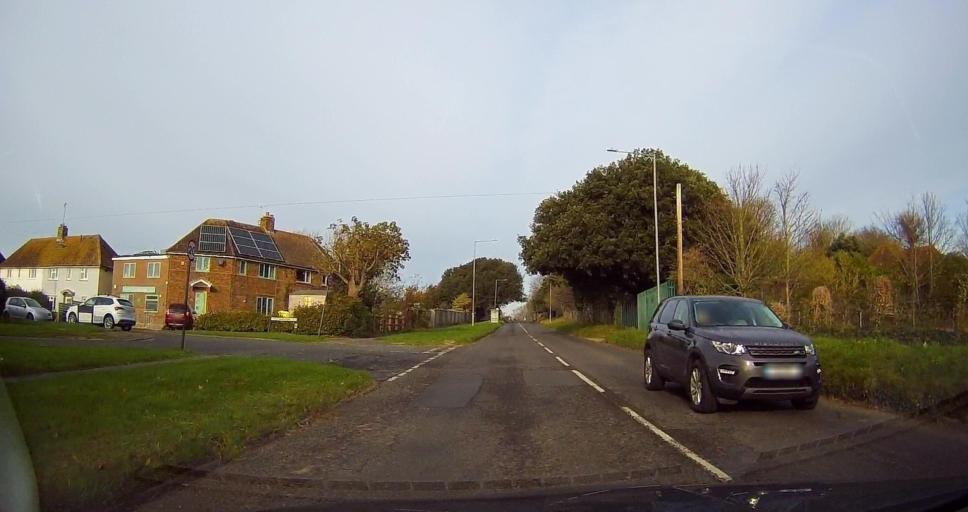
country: GB
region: England
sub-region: Brighton and Hove
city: Rottingdean
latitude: 50.8147
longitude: -0.0631
